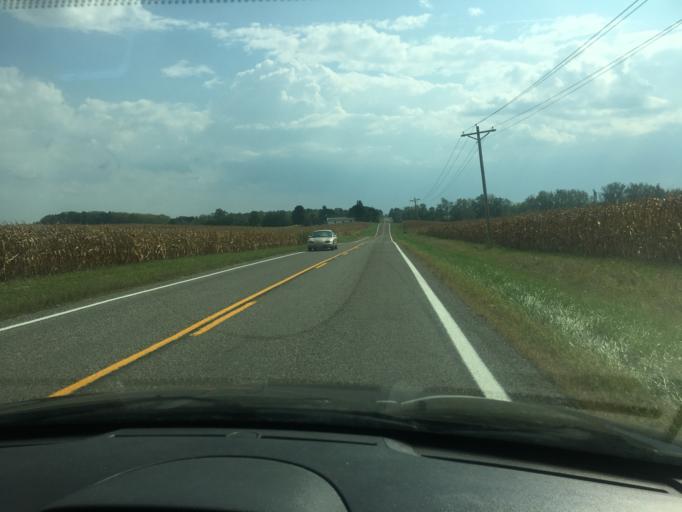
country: US
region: Ohio
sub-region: Champaign County
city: Urbana
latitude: 40.1536
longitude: -83.8335
